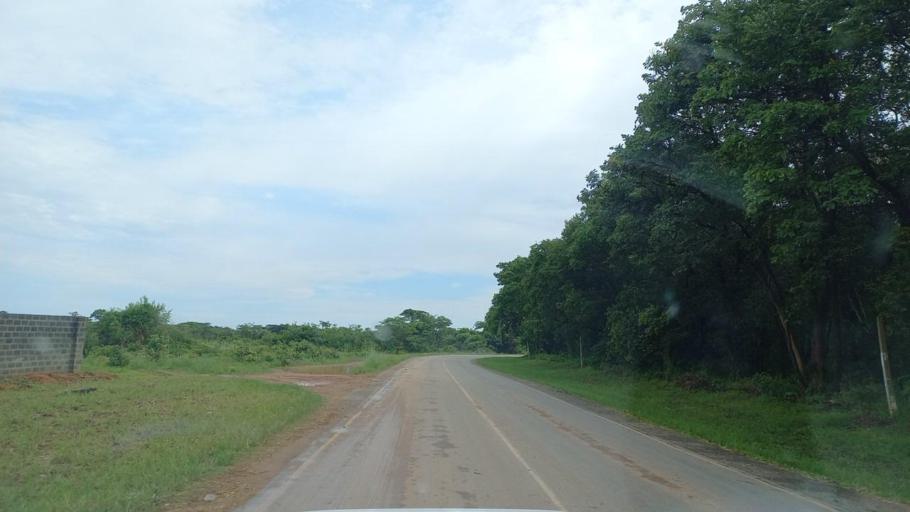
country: ZM
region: Copperbelt
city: Kitwe
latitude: -12.8882
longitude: 28.3109
